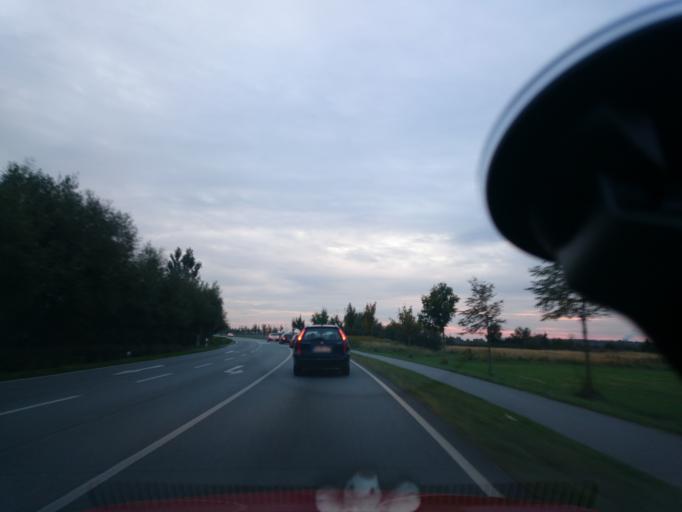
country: DE
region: Mecklenburg-Vorpommern
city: Rovershagen
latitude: 54.1728
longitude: 12.2413
